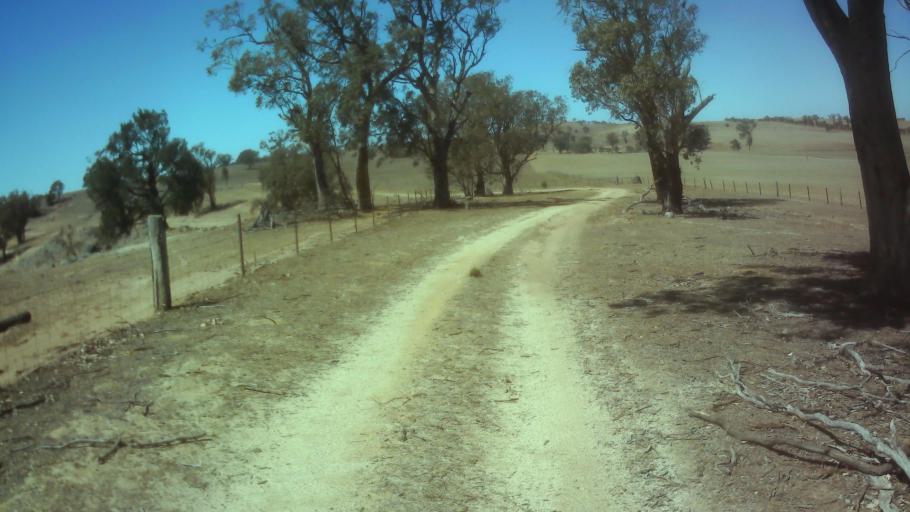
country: AU
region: New South Wales
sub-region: Cowra
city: Cowra
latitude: -33.8916
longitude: 148.5010
